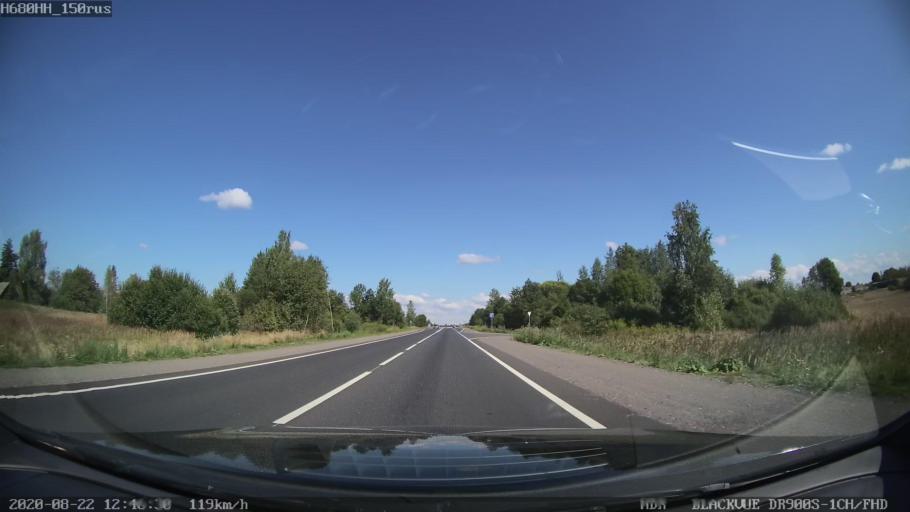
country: RU
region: Tverskaya
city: Rameshki
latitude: 57.4208
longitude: 36.1478
